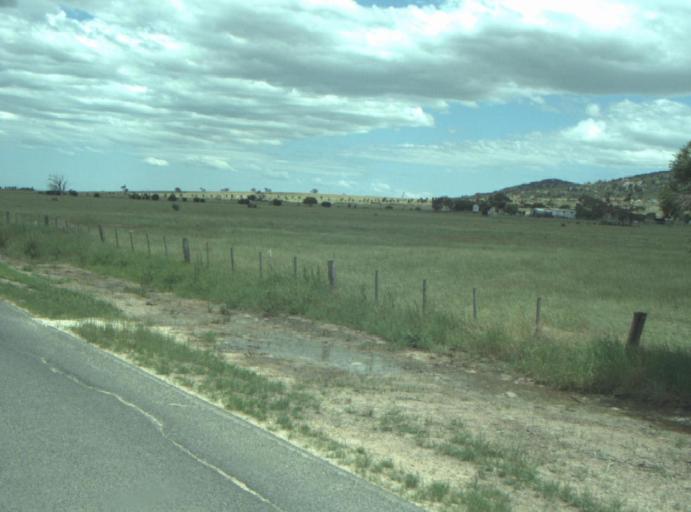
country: AU
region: Victoria
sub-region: Wyndham
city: Little River
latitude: -37.9227
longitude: 144.4638
